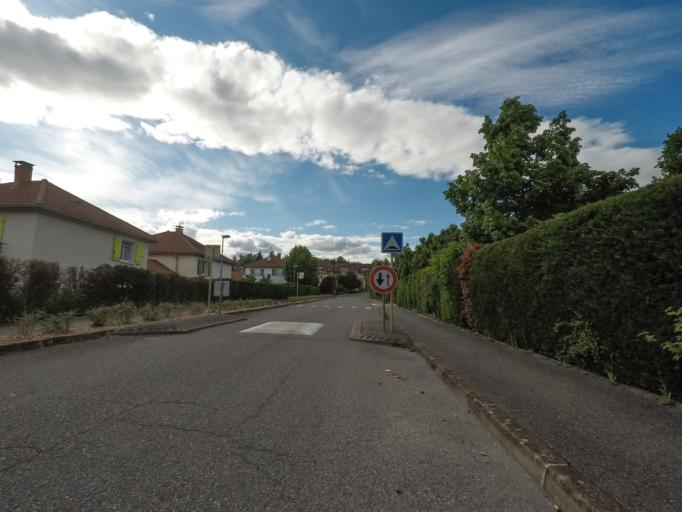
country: CH
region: Geneva
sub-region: Geneva
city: Meyrin
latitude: 46.2501
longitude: 6.0849
